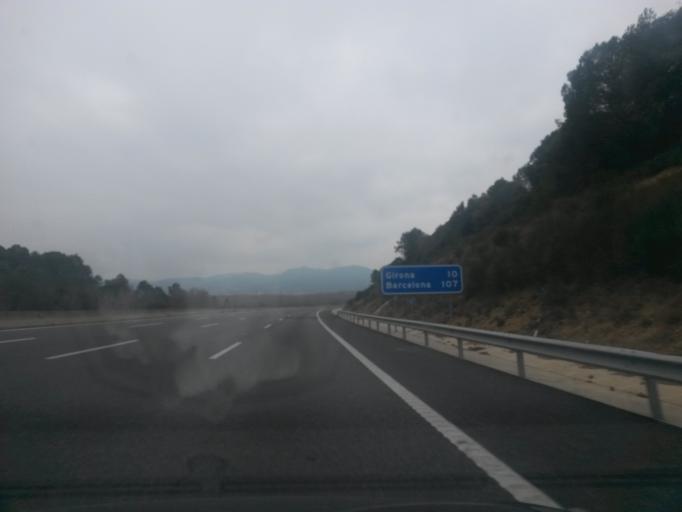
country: ES
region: Catalonia
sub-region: Provincia de Girona
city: Cervia de Ter
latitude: 42.0623
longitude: 2.8854
